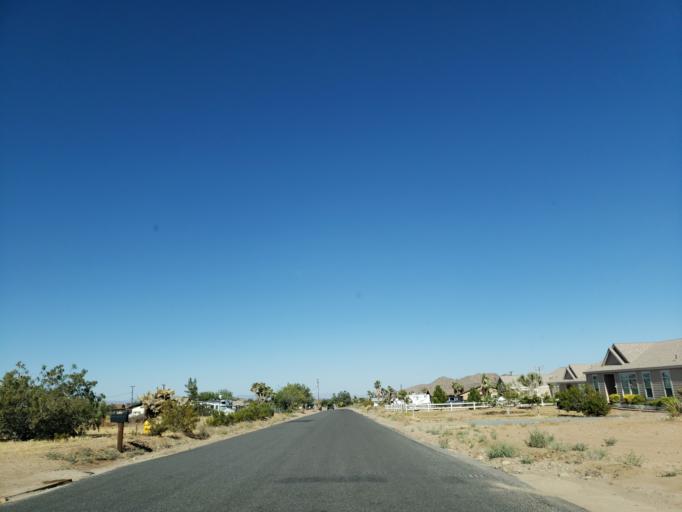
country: US
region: California
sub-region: San Bernardino County
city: Yucca Valley
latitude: 34.1838
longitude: -116.3896
